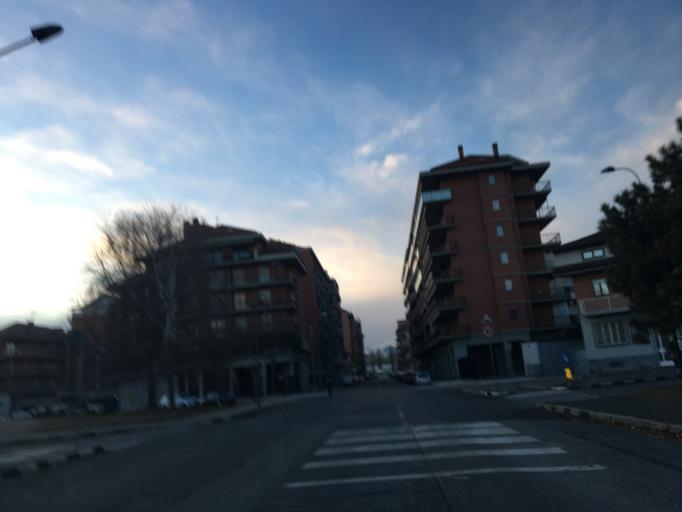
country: IT
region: Piedmont
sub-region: Provincia di Torino
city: Lesna
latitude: 45.0528
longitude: 7.6392
